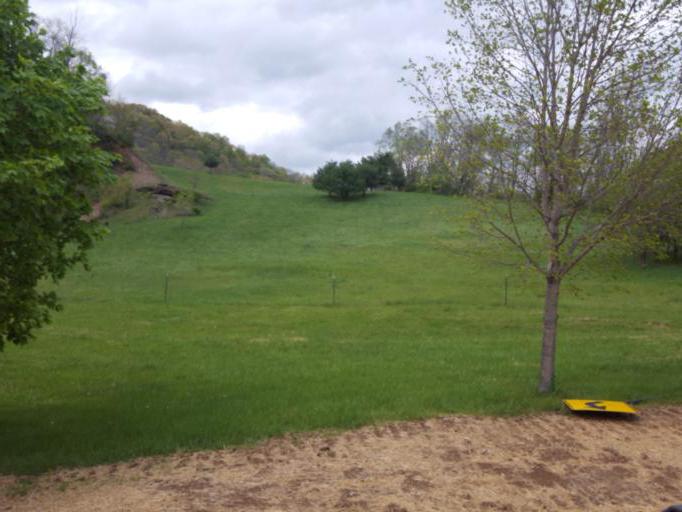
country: US
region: Ohio
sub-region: Ashland County
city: Loudonville
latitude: 40.5444
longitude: -82.2080
